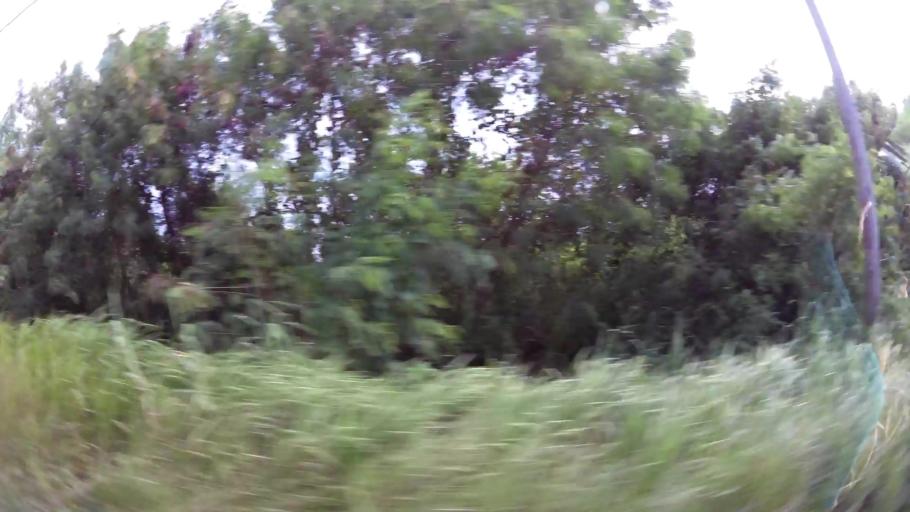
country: SR
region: Paramaribo
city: Paramaribo
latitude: 5.8537
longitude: -55.1535
